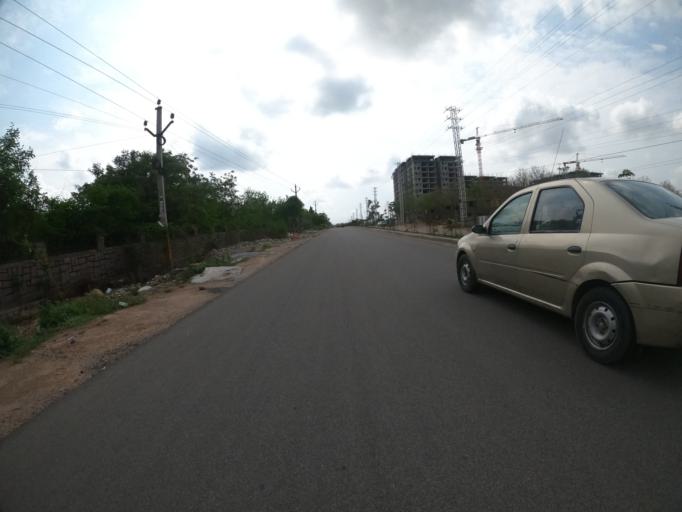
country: IN
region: Telangana
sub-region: Medak
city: Serilingampalle
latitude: 17.3912
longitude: 78.3241
